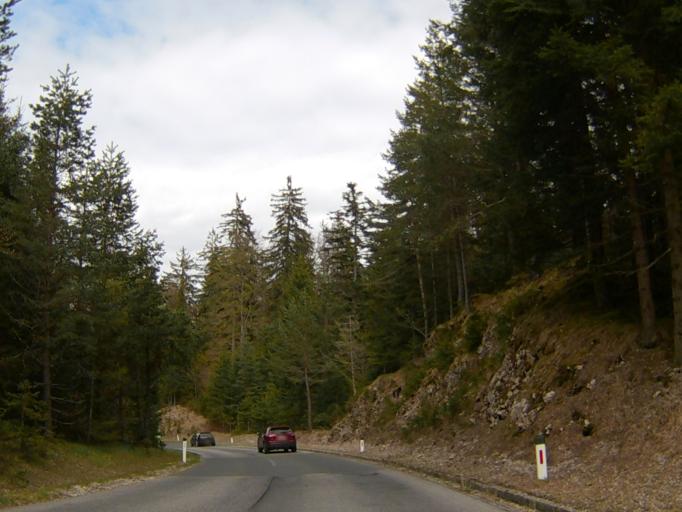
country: AT
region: Carinthia
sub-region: Politischer Bezirk Villach Land
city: Arnoldstein
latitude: 46.5871
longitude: 13.7661
